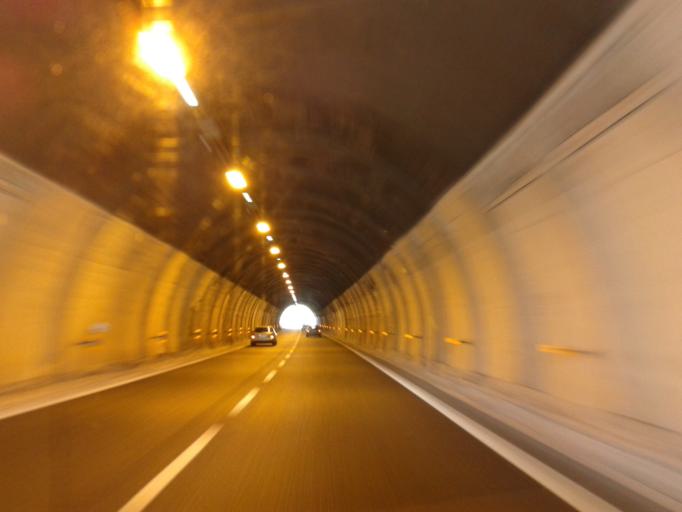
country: IT
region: Liguria
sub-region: Provincia di Genova
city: Chiavari
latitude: 44.3287
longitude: 9.3174
